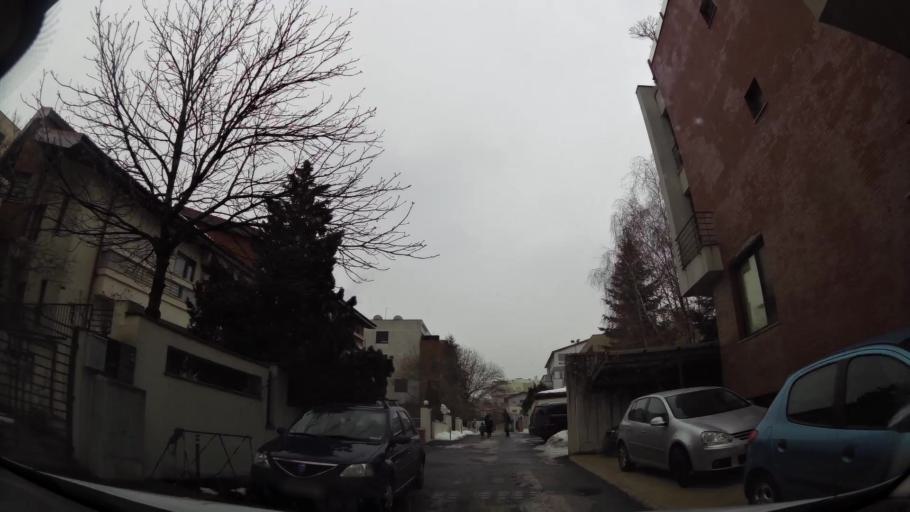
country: RO
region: Bucuresti
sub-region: Municipiul Bucuresti
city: Bucharest
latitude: 44.4835
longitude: 26.0886
